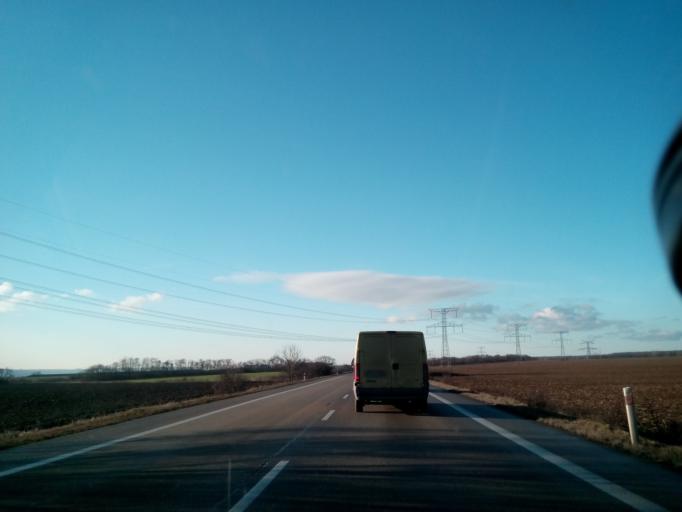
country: SK
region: Kosicky
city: Kosice
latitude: 48.6241
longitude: 21.1553
